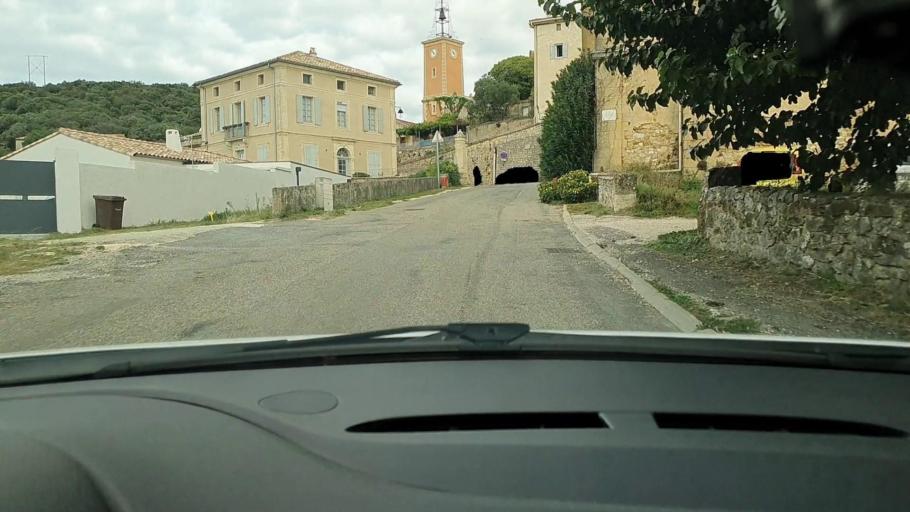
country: FR
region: Languedoc-Roussillon
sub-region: Departement du Gard
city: Montaren-et-Saint-Mediers
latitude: 44.0586
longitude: 4.3212
